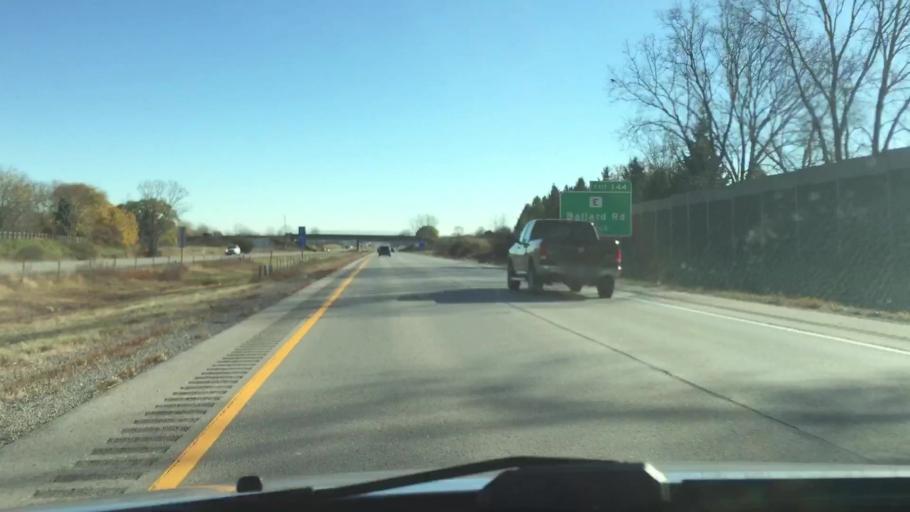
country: US
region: Wisconsin
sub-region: Outagamie County
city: Appleton
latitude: 44.2983
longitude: -88.4011
